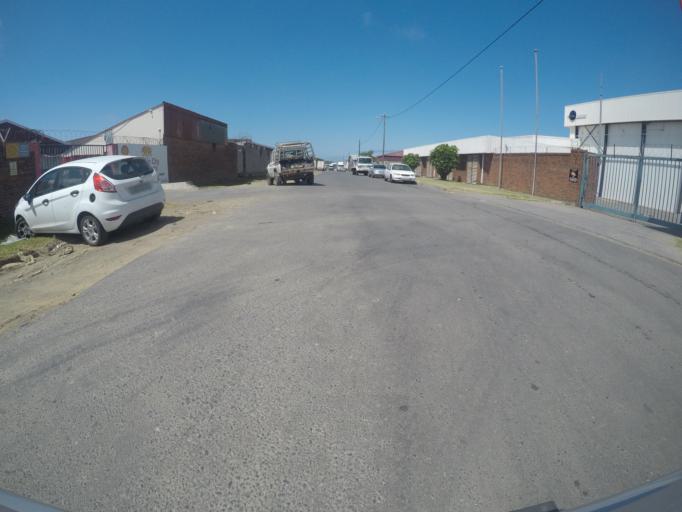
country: ZA
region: Eastern Cape
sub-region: Buffalo City Metropolitan Municipality
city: East London
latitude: -33.0087
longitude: 27.9102
